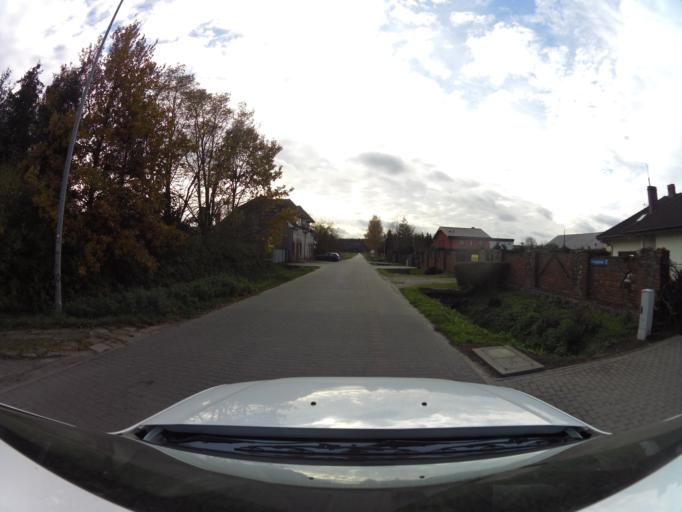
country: PL
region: West Pomeranian Voivodeship
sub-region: Powiat gryficki
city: Gryfice
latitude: 53.9163
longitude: 15.1794
